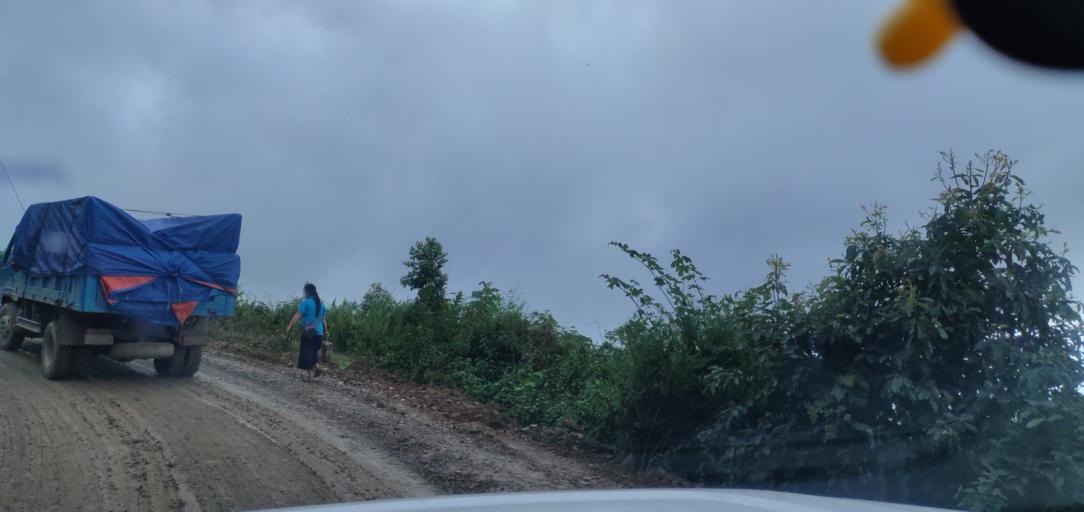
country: LA
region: Phongsali
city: Phongsali
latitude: 21.4215
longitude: 102.1752
